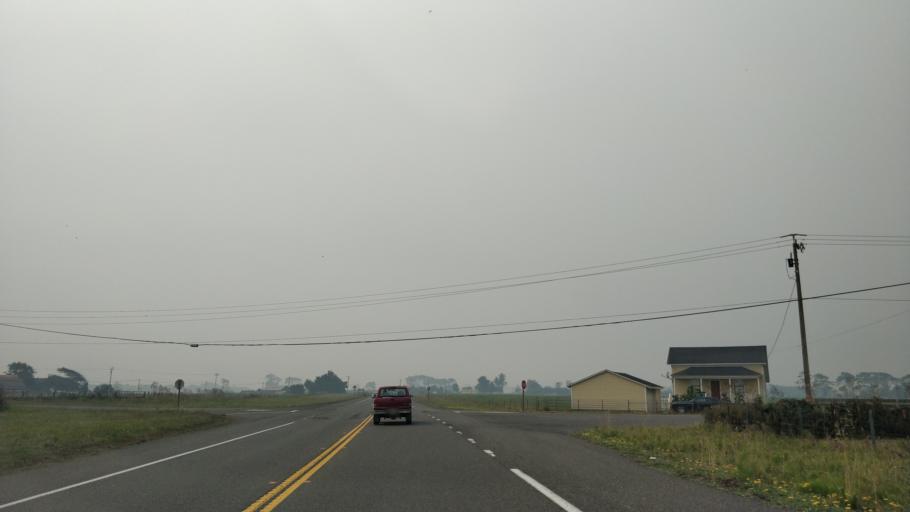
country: US
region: California
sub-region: Humboldt County
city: Ferndale
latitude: 40.5981
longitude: -124.2304
